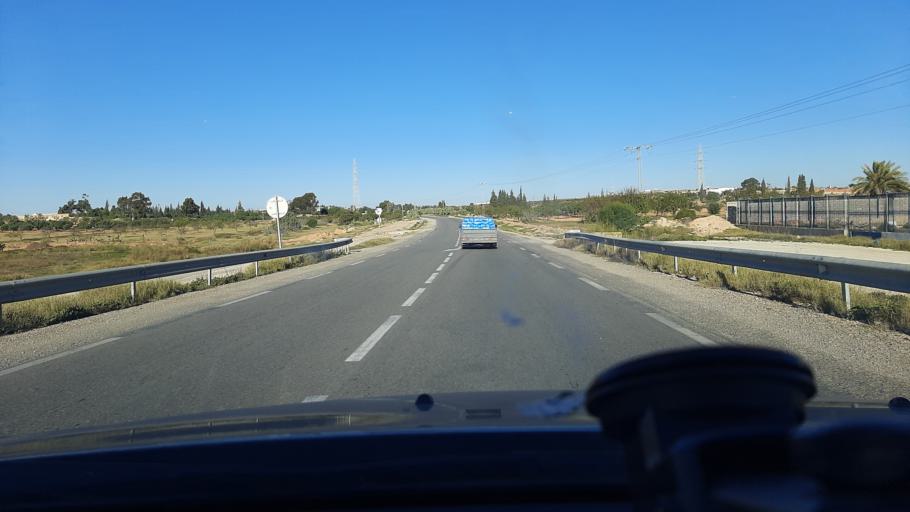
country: TN
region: Safaqis
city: Sfax
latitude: 34.8082
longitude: 10.6246
